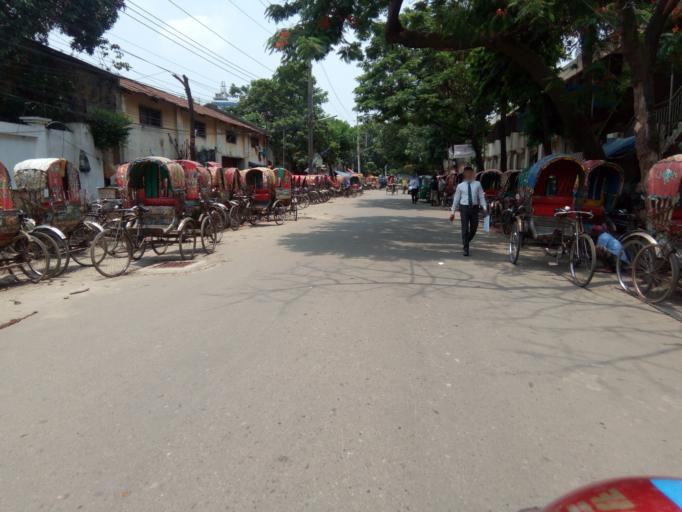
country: BD
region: Dhaka
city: Paltan
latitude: 23.7685
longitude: 90.4025
